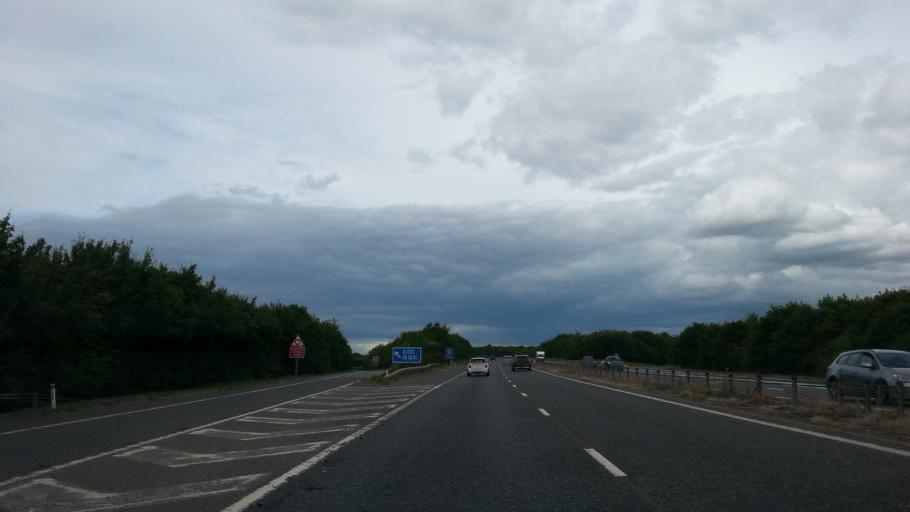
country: GB
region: England
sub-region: Cambridgeshire
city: Duxford
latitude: 52.0724
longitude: 0.1898
